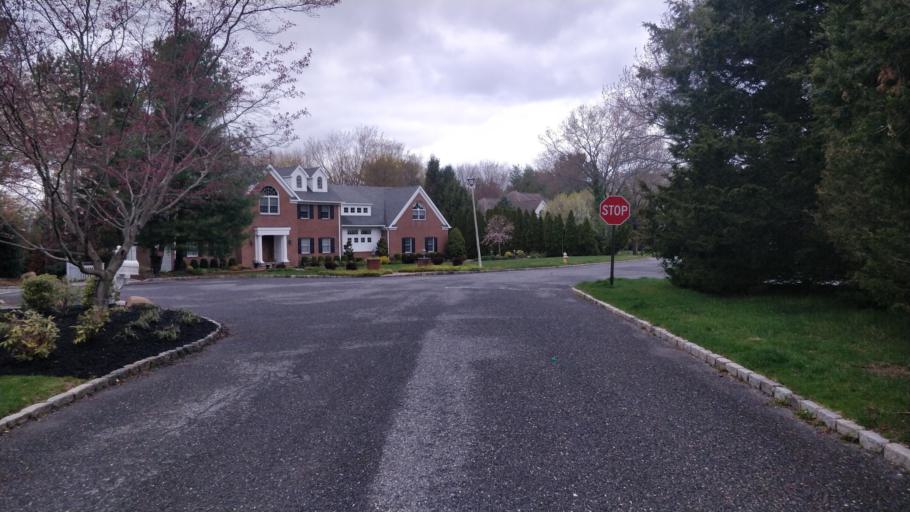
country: US
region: New York
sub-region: Suffolk County
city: East Setauket
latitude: 40.9519
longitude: -73.0918
